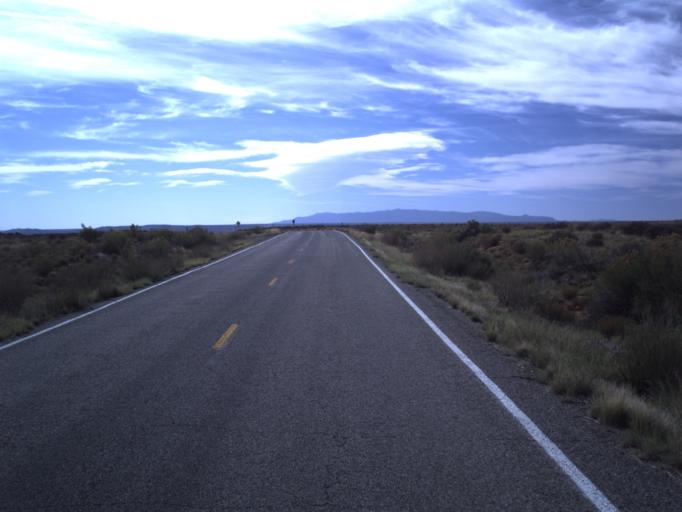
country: US
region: Utah
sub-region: San Juan County
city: Blanding
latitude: 37.3290
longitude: -109.3446
